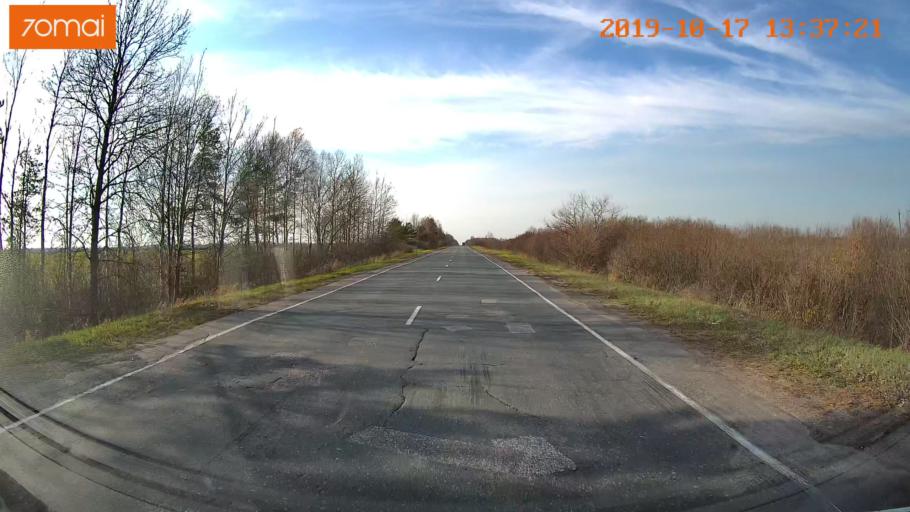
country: RU
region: Rjazan
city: Tuma
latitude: 55.1414
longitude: 40.6414
